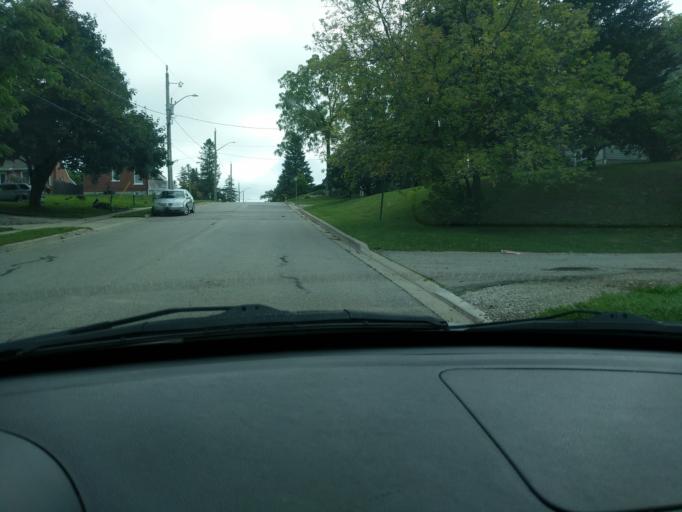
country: CA
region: Ontario
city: Cambridge
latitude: 43.4267
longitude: -80.3133
